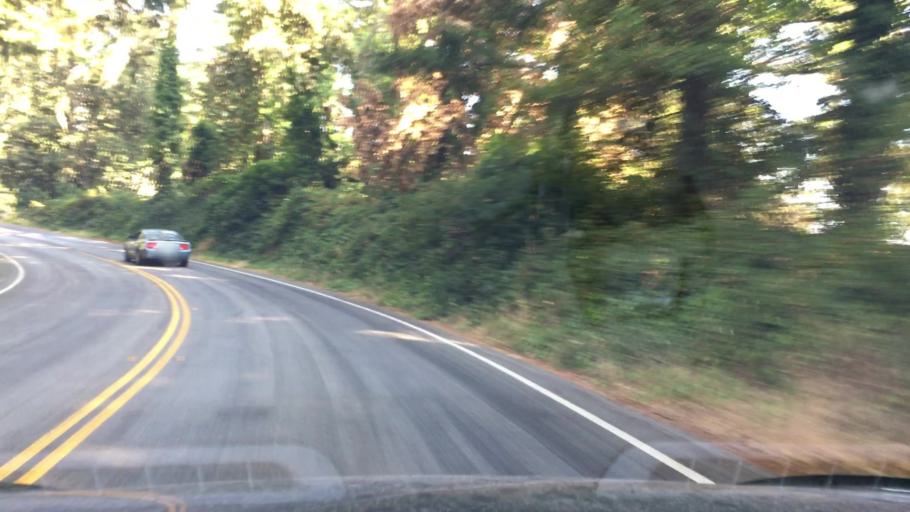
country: US
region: California
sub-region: San Mateo County
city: Portola Valley
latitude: 37.3760
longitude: -122.2627
